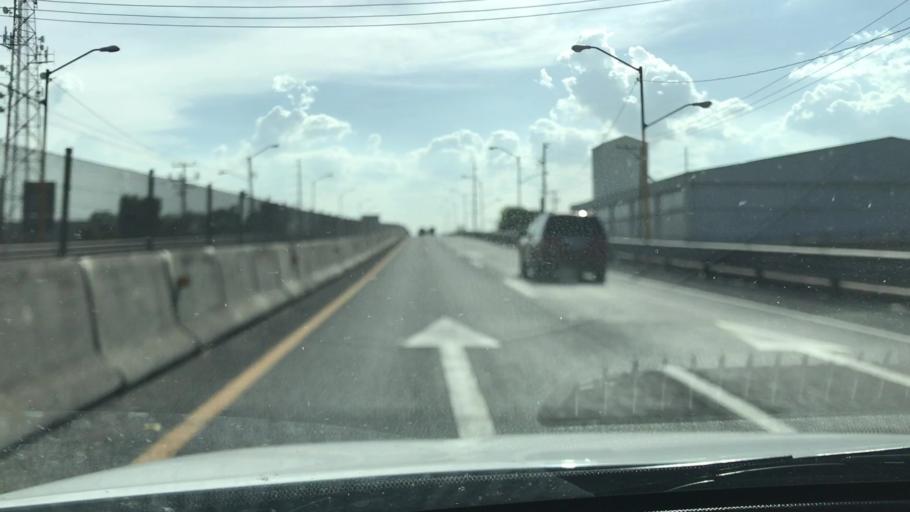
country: MX
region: Guanajuato
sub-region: Cortazar
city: Colonia la Calzada (La Olla)
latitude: 20.5113
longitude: -100.9517
